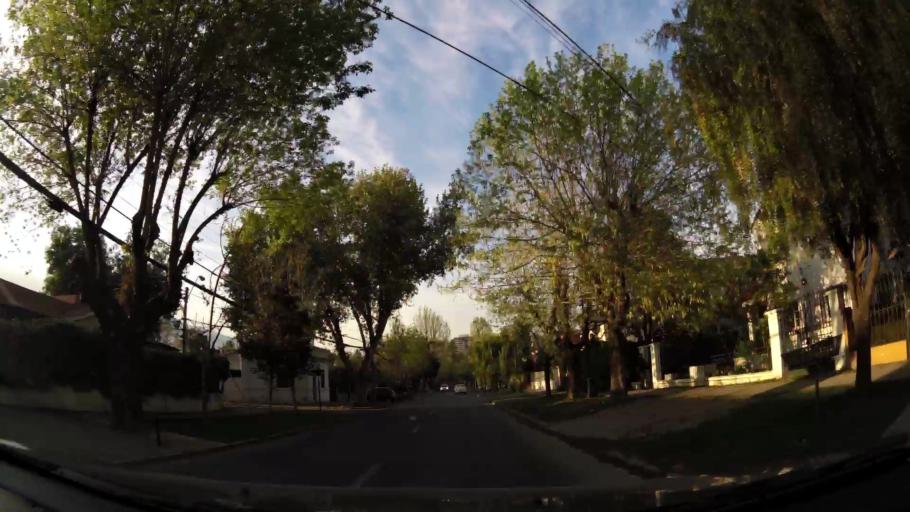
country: CL
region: Santiago Metropolitan
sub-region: Provincia de Santiago
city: Villa Presidente Frei, Nunoa, Santiago, Chile
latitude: -33.4497
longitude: -70.5766
